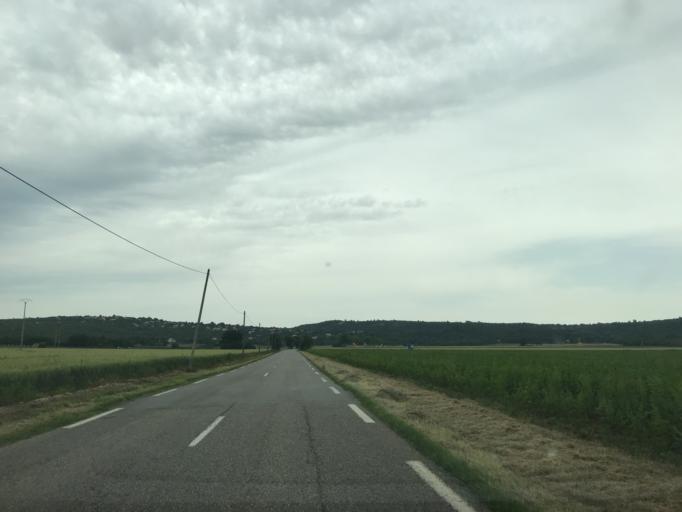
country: FR
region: Provence-Alpes-Cote d'Azur
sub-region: Departement du Var
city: Ginasservis
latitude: 43.6508
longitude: 5.8407
